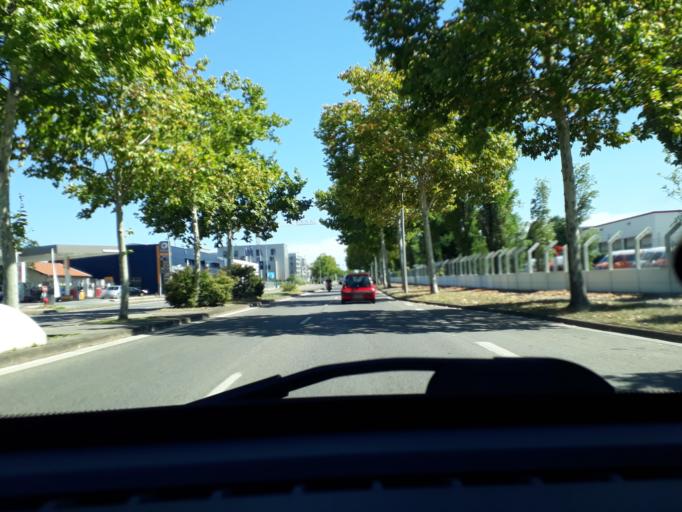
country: FR
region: Rhone-Alpes
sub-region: Departement du Rhone
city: Saint-Priest
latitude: 45.7014
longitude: 4.9179
